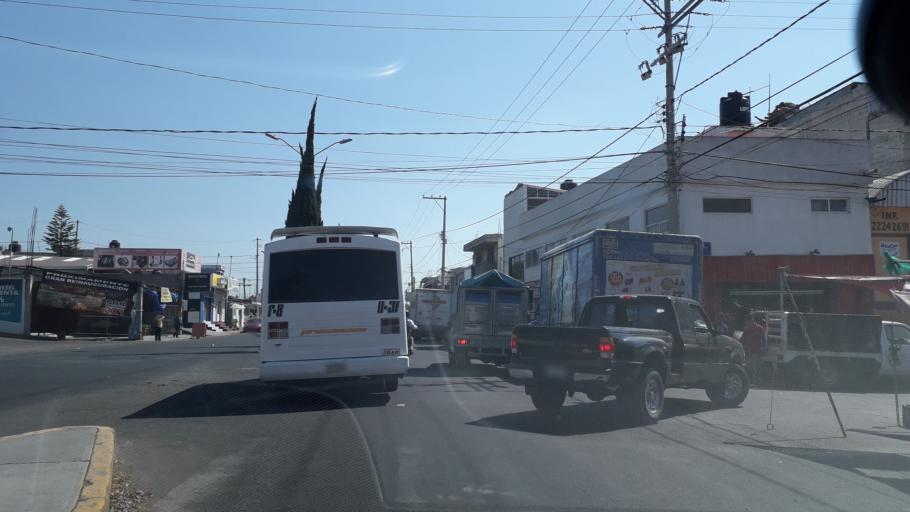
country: MX
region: Puebla
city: Puebla
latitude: 18.9910
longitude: -98.2141
